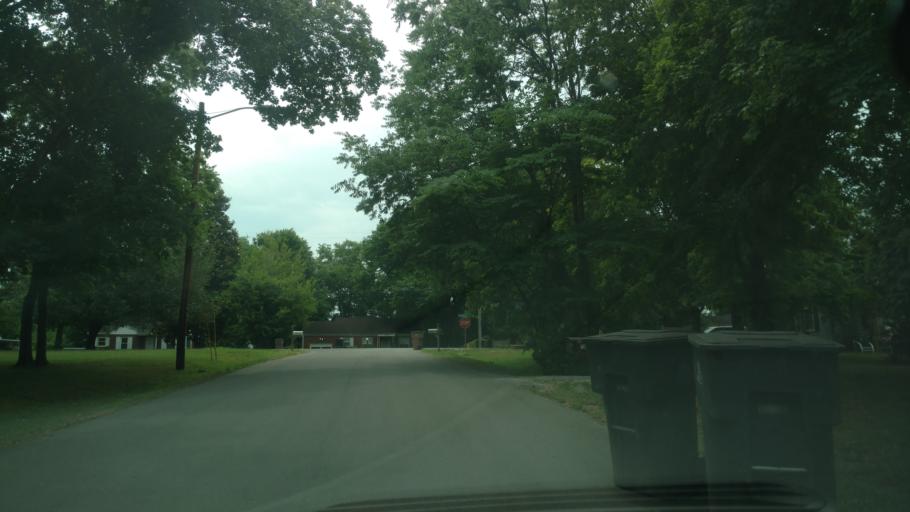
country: US
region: Tennessee
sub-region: Davidson County
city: Nashville
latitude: 36.2020
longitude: -86.7175
